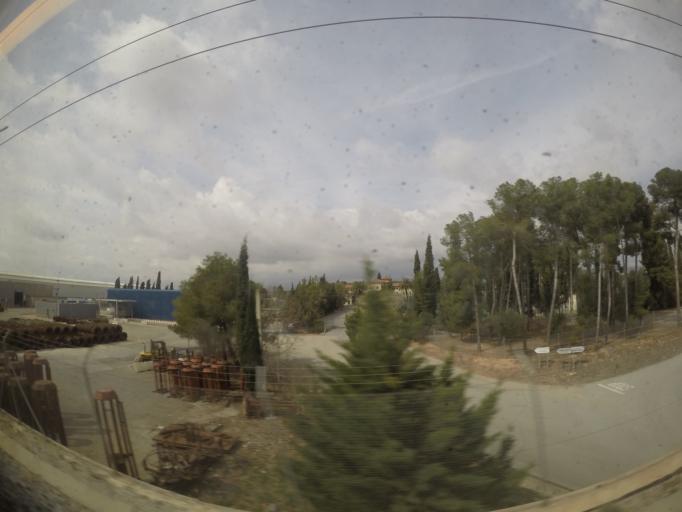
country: ES
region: Catalonia
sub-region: Provincia de Tarragona
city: Santa Oliva
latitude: 41.2632
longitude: 1.5878
